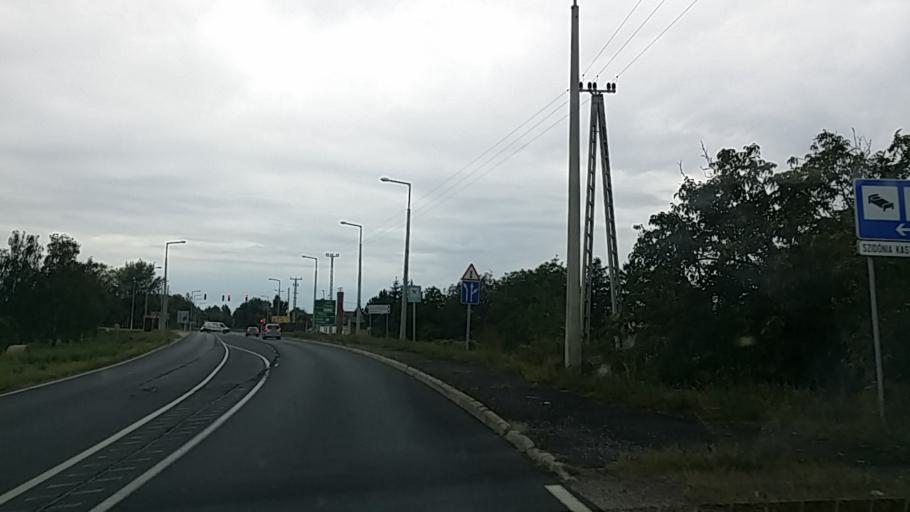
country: HU
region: Gyor-Moson-Sopron
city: Fertoszentmiklos
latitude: 47.5910
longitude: 16.8772
